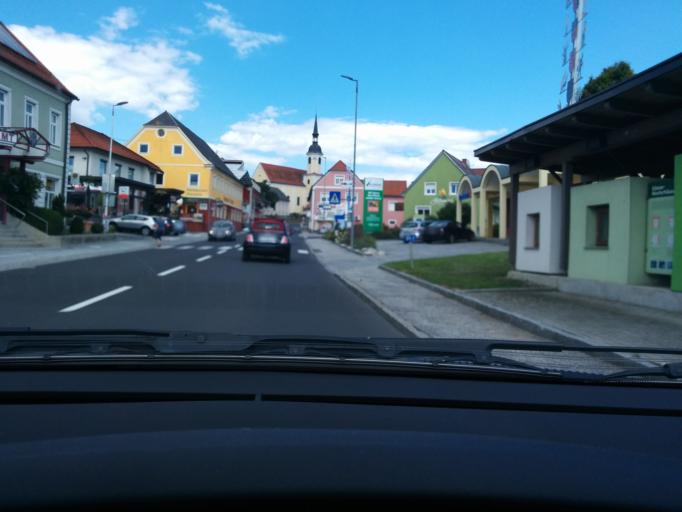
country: AT
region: Styria
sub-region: Politischer Bezirk Hartberg-Fuerstenfeld
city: Kaindorf
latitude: 47.2247
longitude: 15.9090
